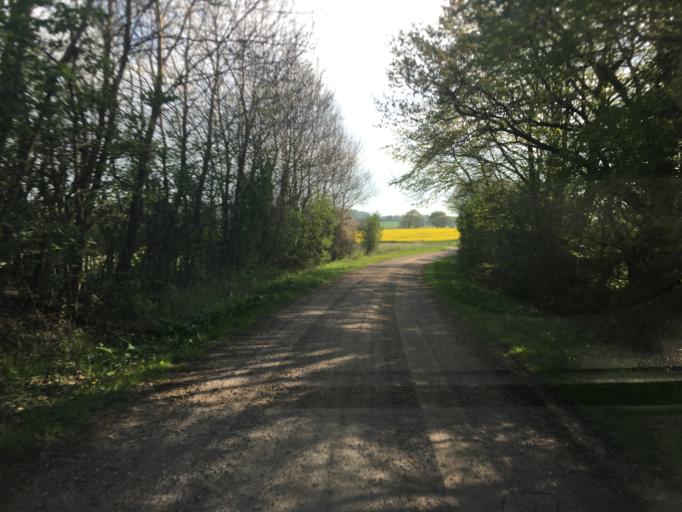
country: DK
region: South Denmark
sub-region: Haderslev Kommune
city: Vojens
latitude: 55.1841
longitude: 9.3927
